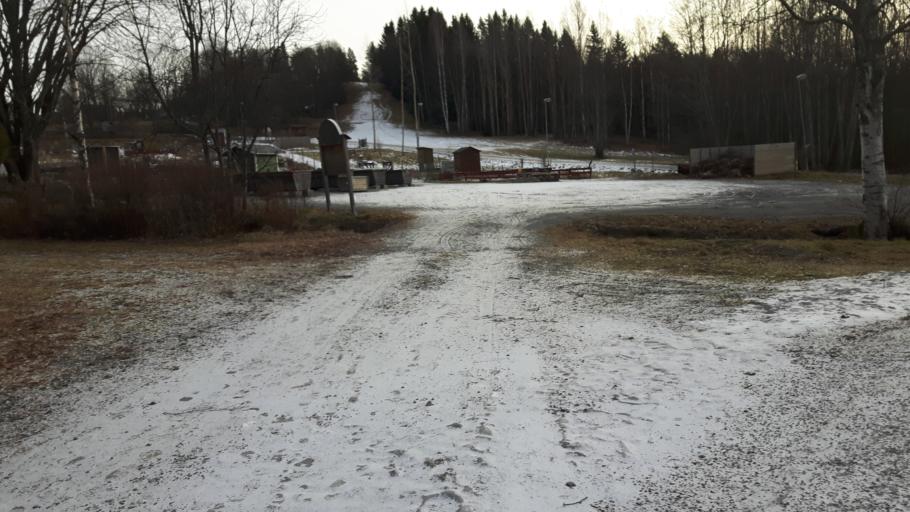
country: SE
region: Vaesternorrland
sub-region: Haernoesands Kommun
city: Haernoesand
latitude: 62.6310
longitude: 17.9655
